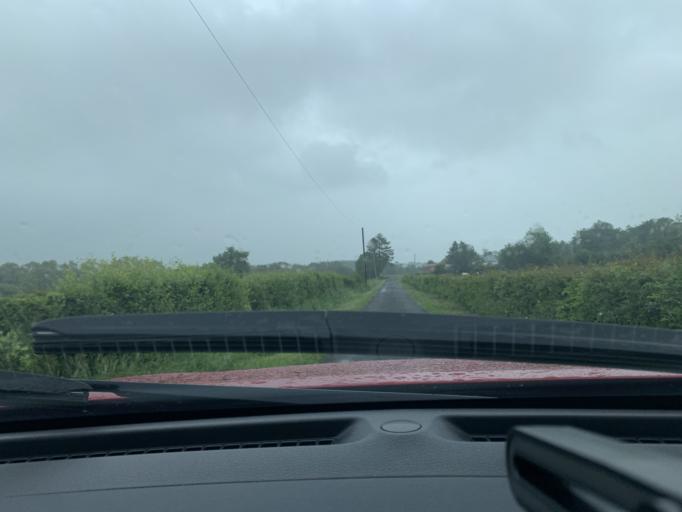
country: GB
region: Northern Ireland
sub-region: Fermanagh District
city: Enniskillen
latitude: 54.2738
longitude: -7.7395
